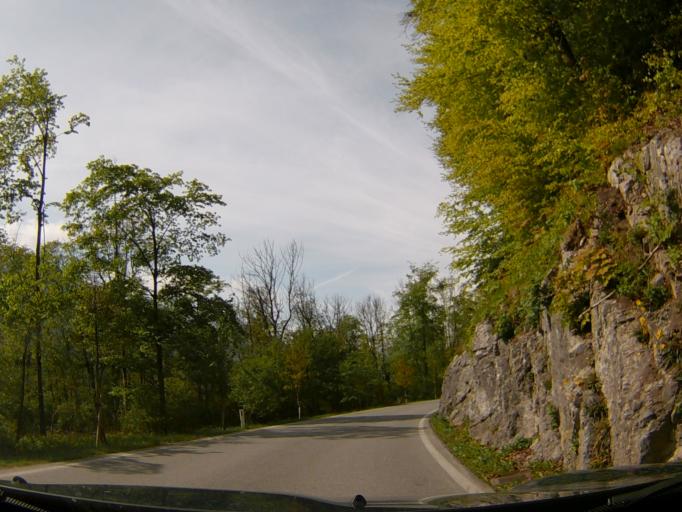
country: AT
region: Tyrol
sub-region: Politischer Bezirk Schwaz
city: Buch bei Jenbach
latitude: 47.3856
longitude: 11.7463
